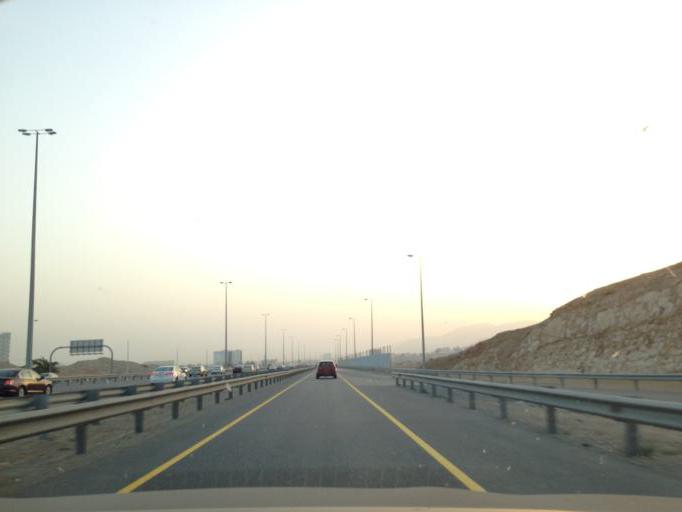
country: OM
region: Muhafazat Masqat
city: Bawshar
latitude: 23.5615
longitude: 58.3421
